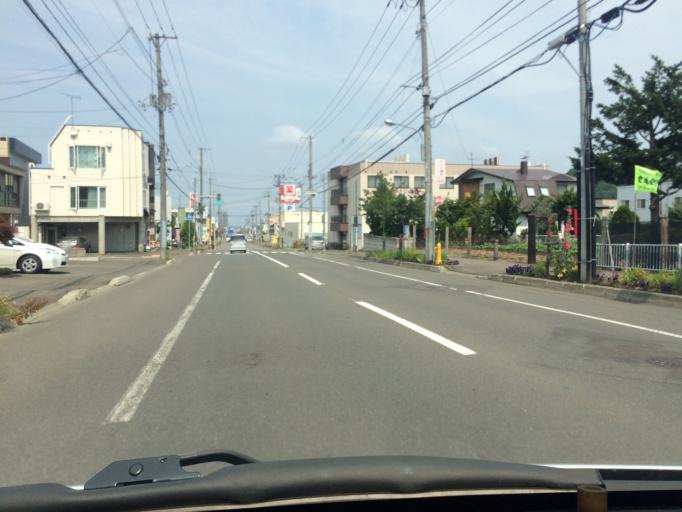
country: JP
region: Hokkaido
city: Sapporo
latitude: 43.0648
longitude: 141.2687
